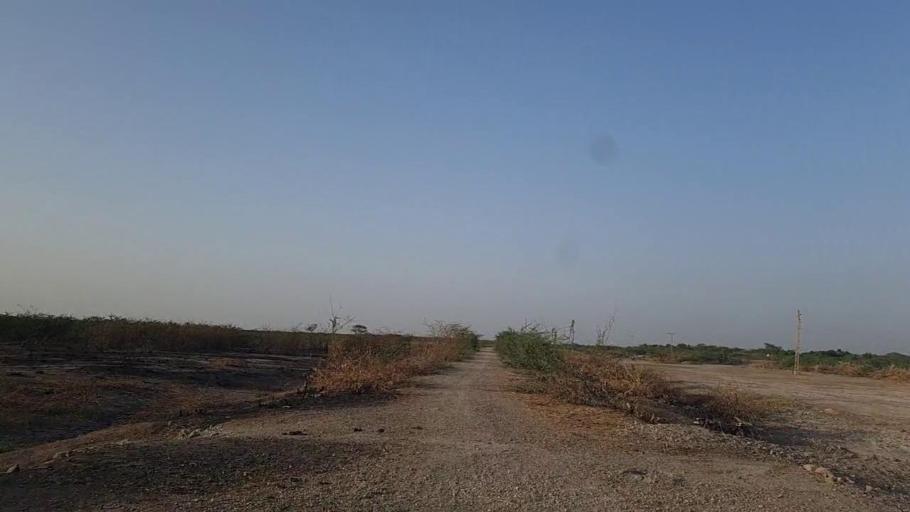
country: PK
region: Sindh
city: Naukot
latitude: 24.6446
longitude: 69.2520
